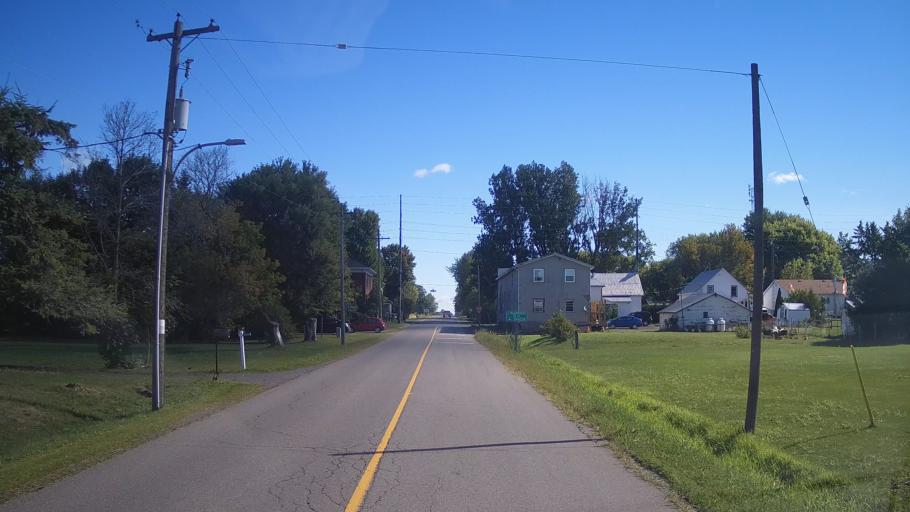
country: CA
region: Ontario
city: Prescott
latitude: 44.9232
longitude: -75.3487
